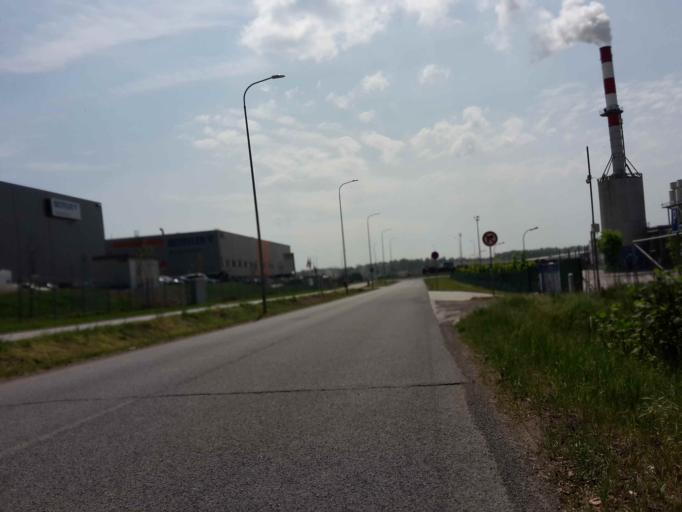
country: SK
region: Bratislavsky
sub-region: Okres Malacky
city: Malacky
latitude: 48.4199
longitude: 17.0354
